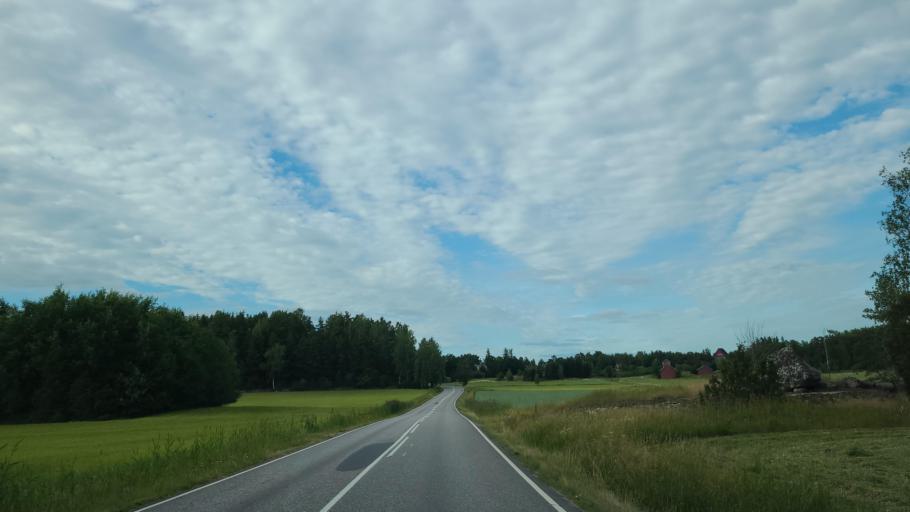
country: FI
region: Varsinais-Suomi
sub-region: Turku
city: Rymaettylae
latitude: 60.3495
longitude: 21.9572
